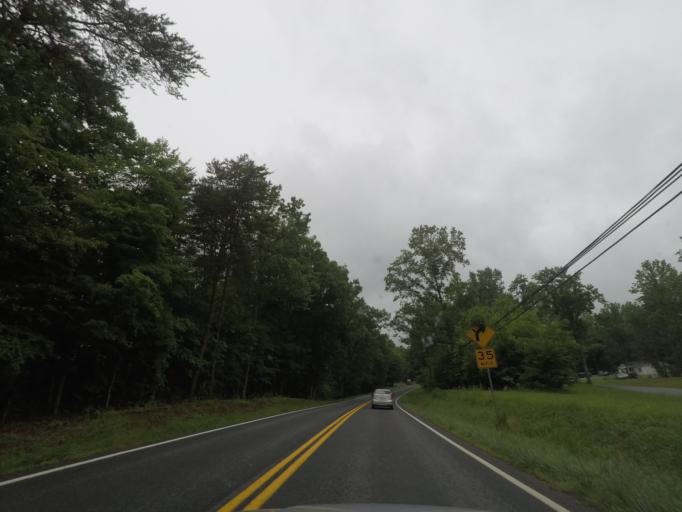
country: US
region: Virginia
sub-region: Fluvanna County
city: Palmyra
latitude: 37.8771
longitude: -78.2624
